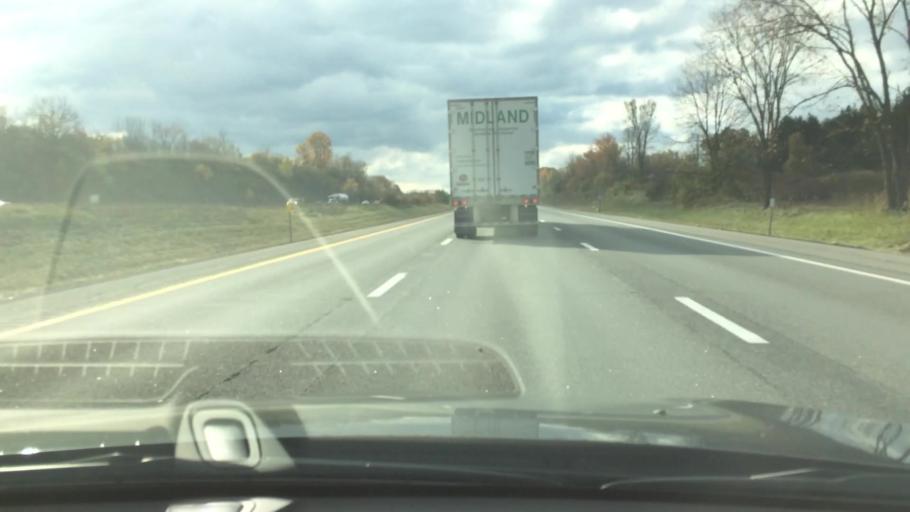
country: US
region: New York
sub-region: Saratoga County
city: Ballston Spa
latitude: 42.9902
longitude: -73.8039
